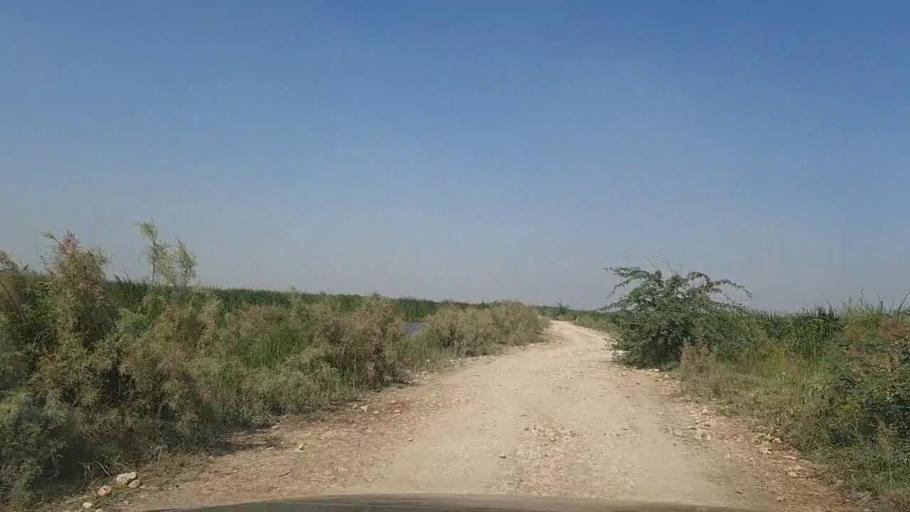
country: PK
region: Sindh
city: Daro Mehar
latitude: 24.8122
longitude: 68.1530
